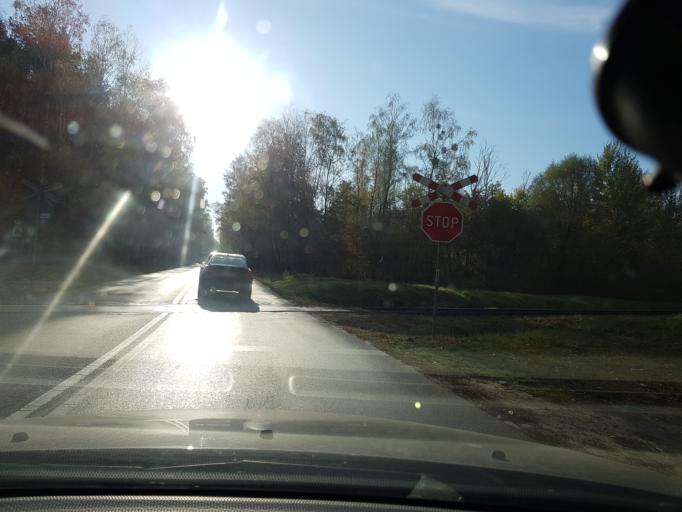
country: PL
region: Masovian Voivodeship
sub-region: Powiat warszawski zachodni
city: Babice
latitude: 52.2702
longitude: 20.8736
